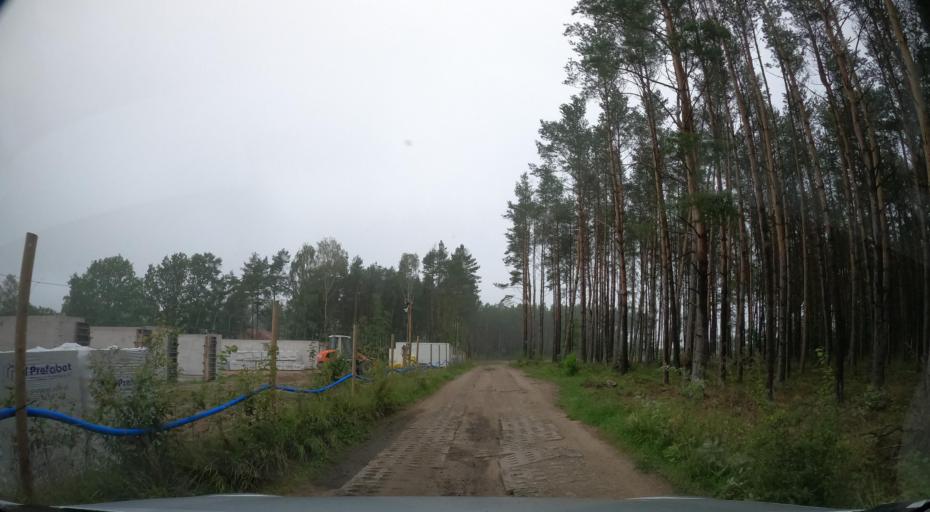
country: PL
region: Pomeranian Voivodeship
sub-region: Powiat kartuski
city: Chwaszczyno
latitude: 54.4356
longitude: 18.4165
